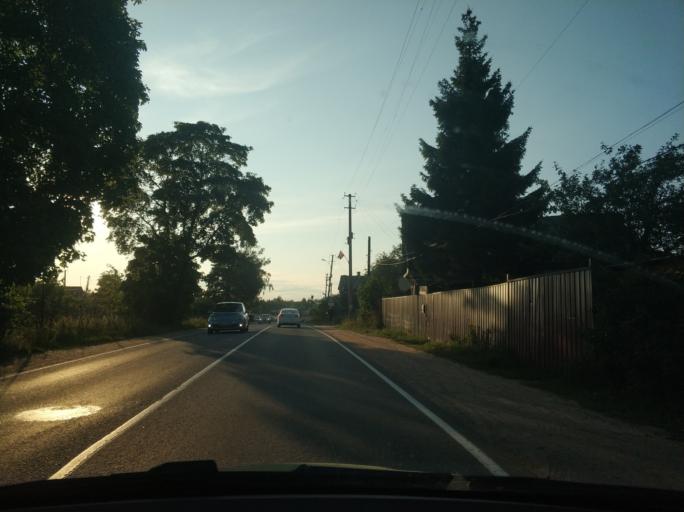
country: RU
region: Leningrad
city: Borisova Griva
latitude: 60.0871
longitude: 31.0213
